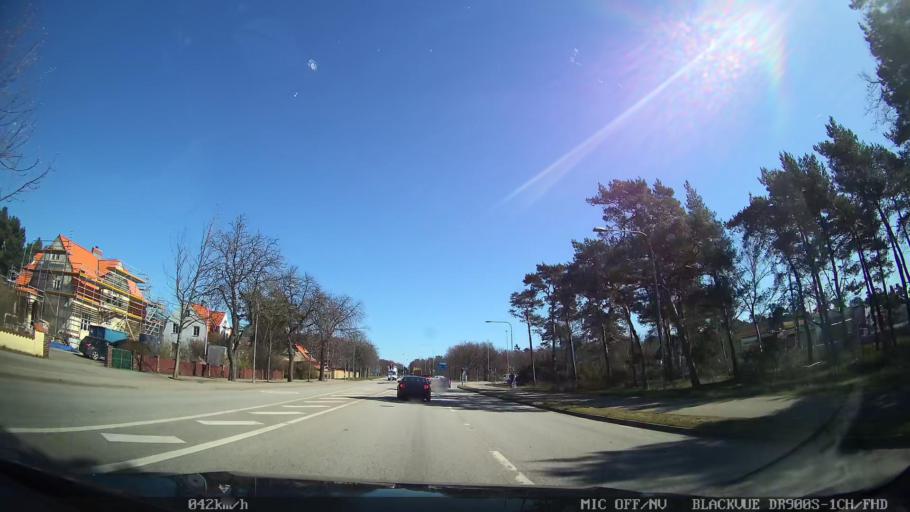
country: SE
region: Skane
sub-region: Ystads Kommun
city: Ystad
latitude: 55.4292
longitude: 13.8393
